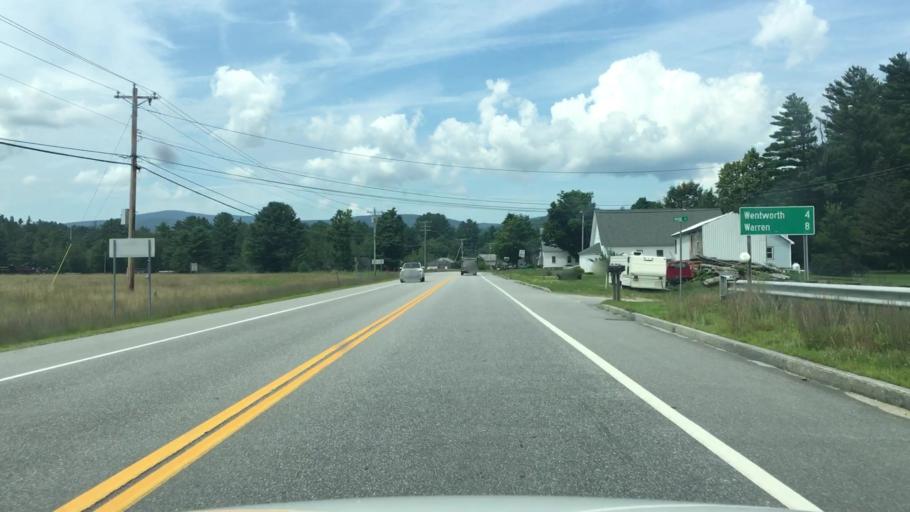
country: US
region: New Hampshire
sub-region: Grafton County
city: Rumney
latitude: 43.8200
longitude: -71.8857
